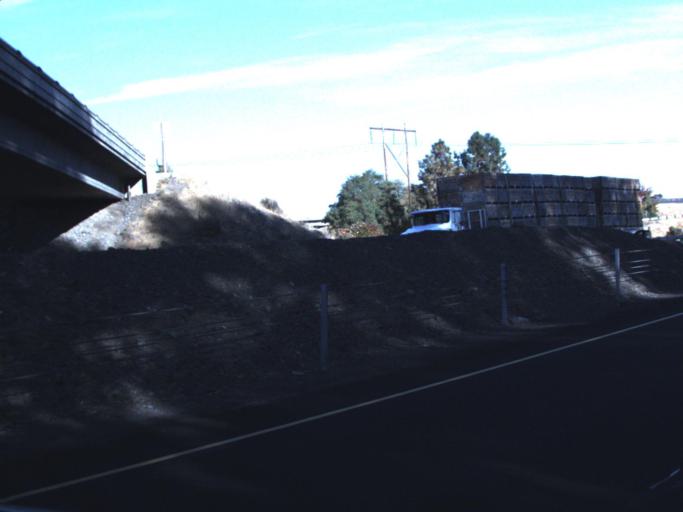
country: US
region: Washington
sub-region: Yakima County
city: Union Gap
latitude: 46.5366
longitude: -120.4713
